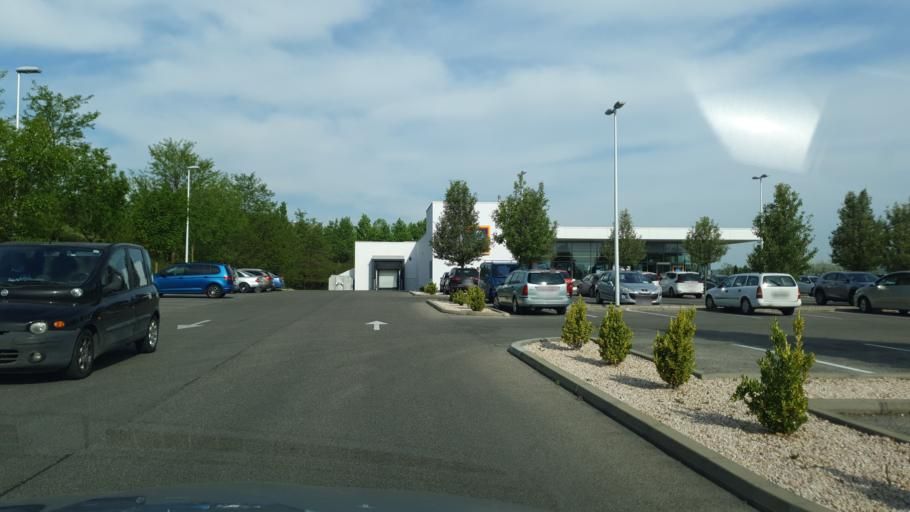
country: HU
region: Pest
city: Toeroekbalint
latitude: 47.4444
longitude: 18.8854
